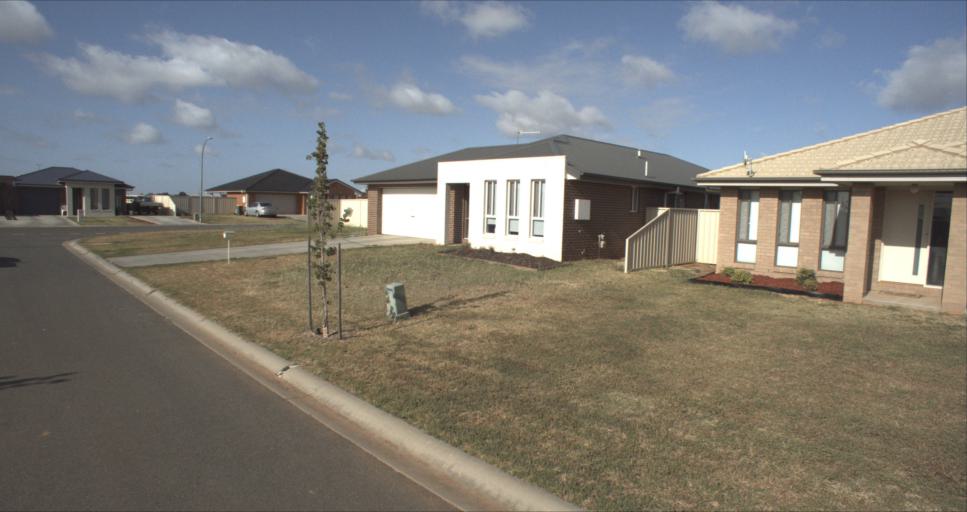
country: AU
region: New South Wales
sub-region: Leeton
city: Leeton
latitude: -34.5700
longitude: 146.4005
